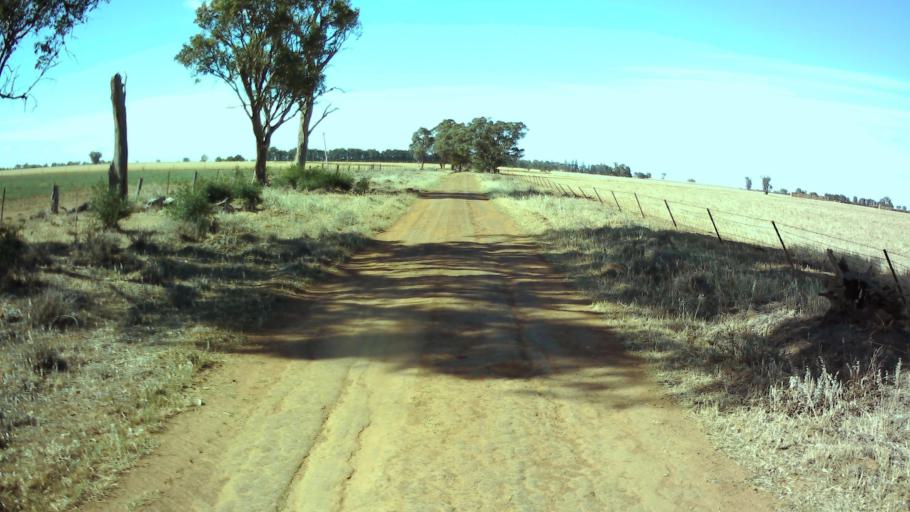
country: AU
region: New South Wales
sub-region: Weddin
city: Grenfell
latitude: -34.0528
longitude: 148.2686
